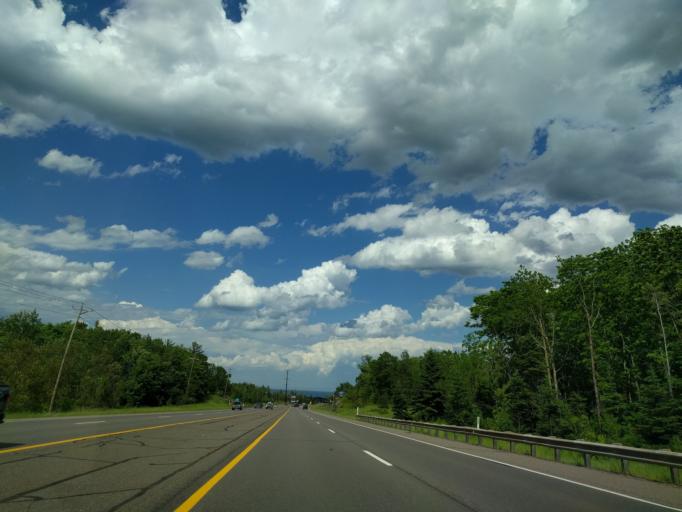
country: US
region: Michigan
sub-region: Marquette County
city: Trowbridge Park
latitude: 46.5448
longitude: -87.4808
